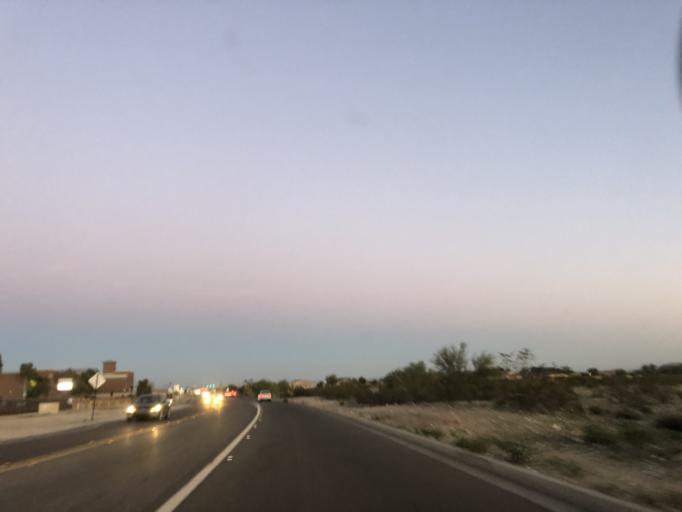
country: US
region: Arizona
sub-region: Maricopa County
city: Citrus Park
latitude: 33.4938
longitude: -112.4947
